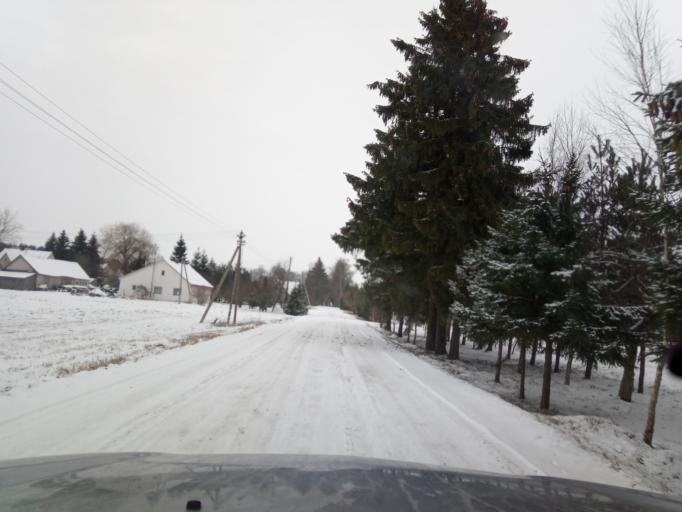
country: LT
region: Panevezys
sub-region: Panevezys City
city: Panevezys
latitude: 55.6187
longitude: 24.3659
